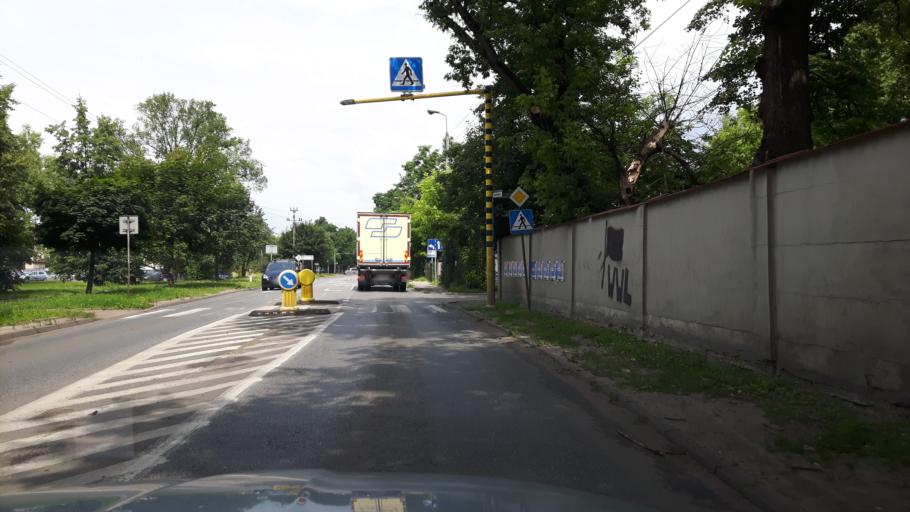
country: PL
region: Masovian Voivodeship
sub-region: Powiat wolominski
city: Nowe Lipiny
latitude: 52.3511
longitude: 21.2623
